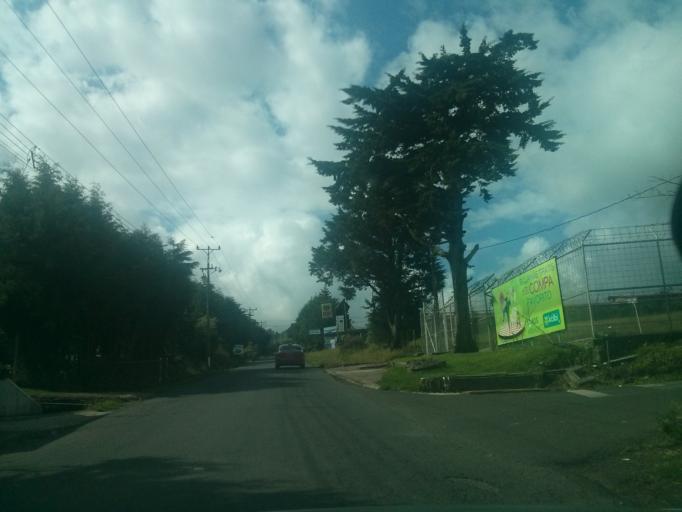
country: CR
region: Alajuela
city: Sabanilla
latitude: 10.1492
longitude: -84.1946
